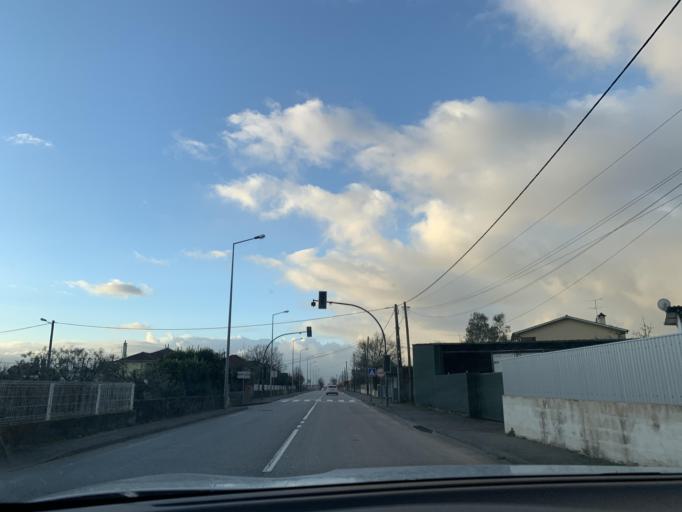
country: PT
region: Viseu
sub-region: Concelho de Tondela
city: Tondela
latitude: 40.4923
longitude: -8.0885
